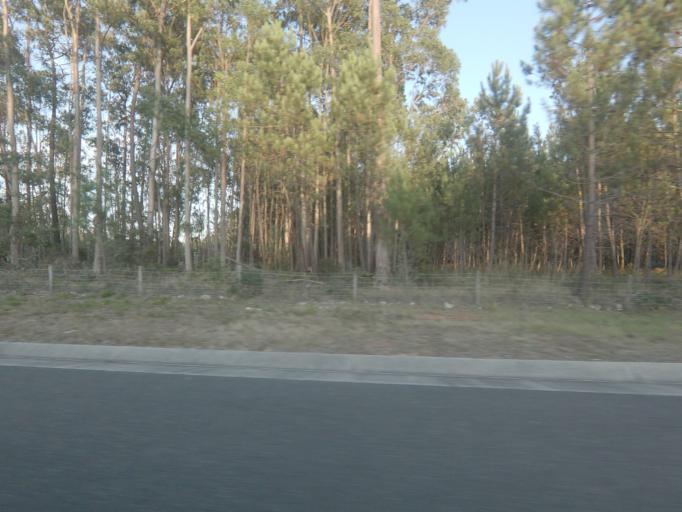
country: PT
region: Leiria
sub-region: Leiria
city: Santa Catarina da Serra
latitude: 39.6450
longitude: -8.6978
